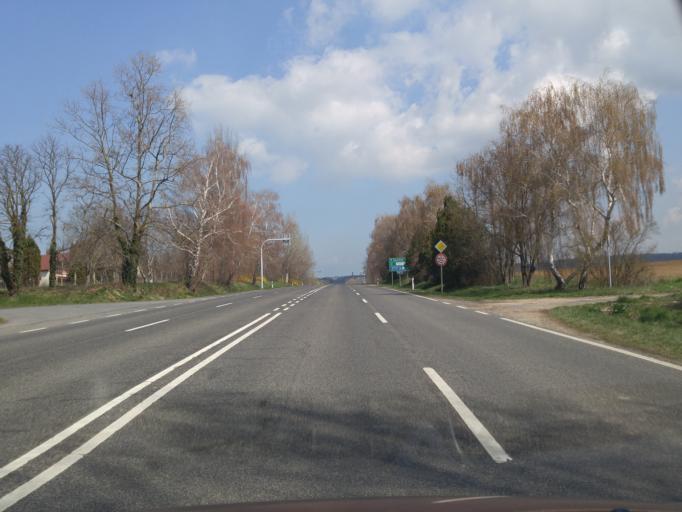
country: HU
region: Somogy
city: Balatonszarszo
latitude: 46.8299
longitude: 17.8429
